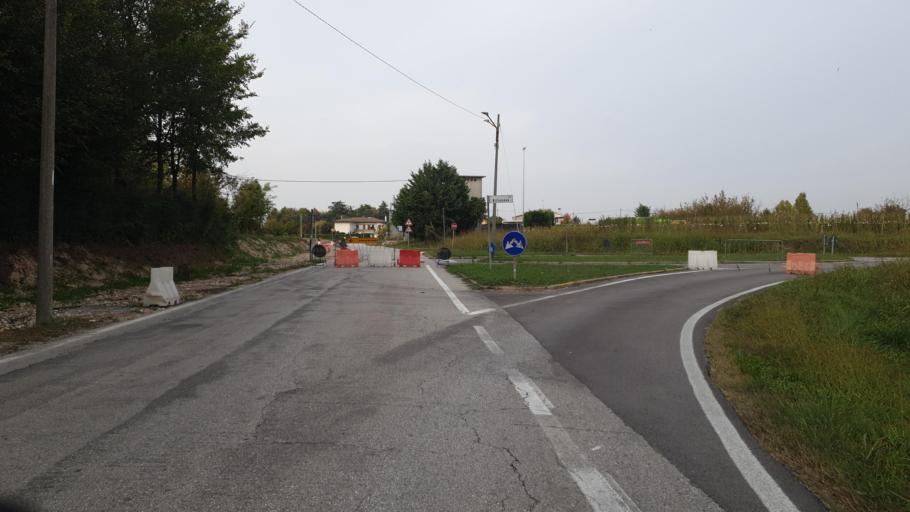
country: IT
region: Veneto
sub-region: Provincia di Padova
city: Villatora
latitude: 45.3878
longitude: 11.9779
